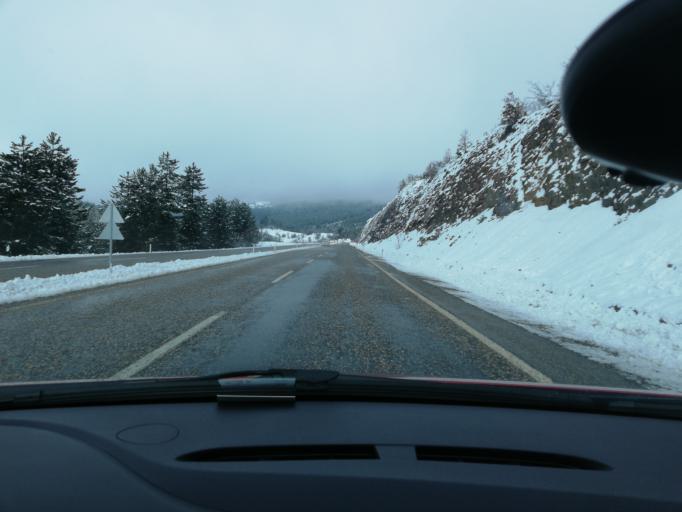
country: TR
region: Kastamonu
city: Akkaya
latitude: 41.2822
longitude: 33.4568
